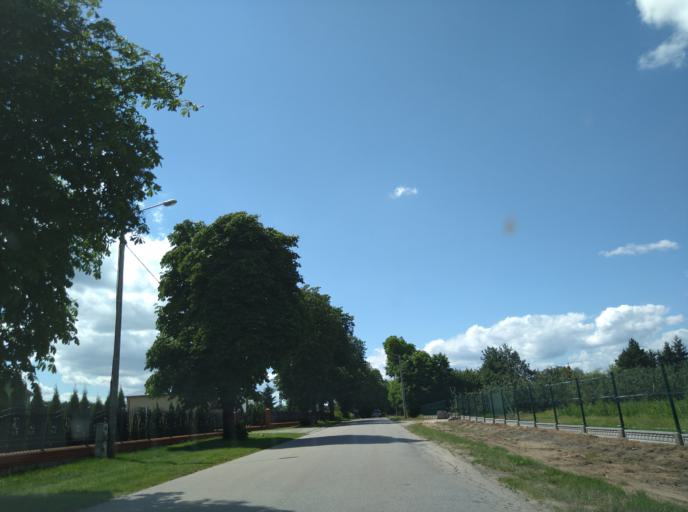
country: PL
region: Masovian Voivodeship
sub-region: Powiat bialobrzeski
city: Promna
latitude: 51.6715
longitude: 20.9283
